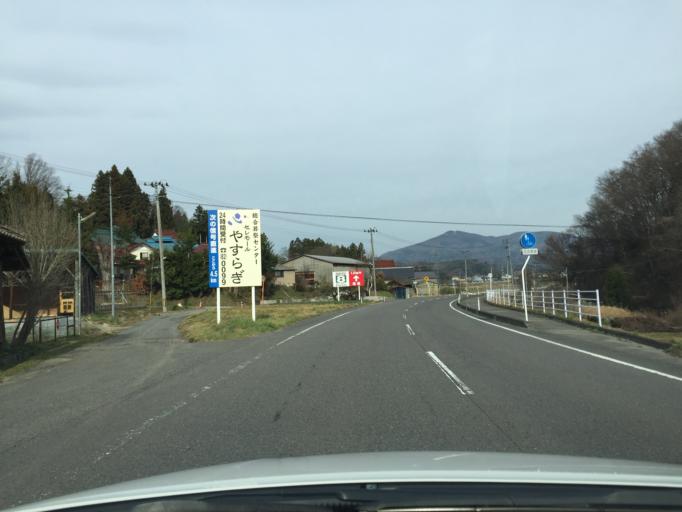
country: JP
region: Fukushima
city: Funehikimachi-funehiki
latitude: 37.4248
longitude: 140.5858
